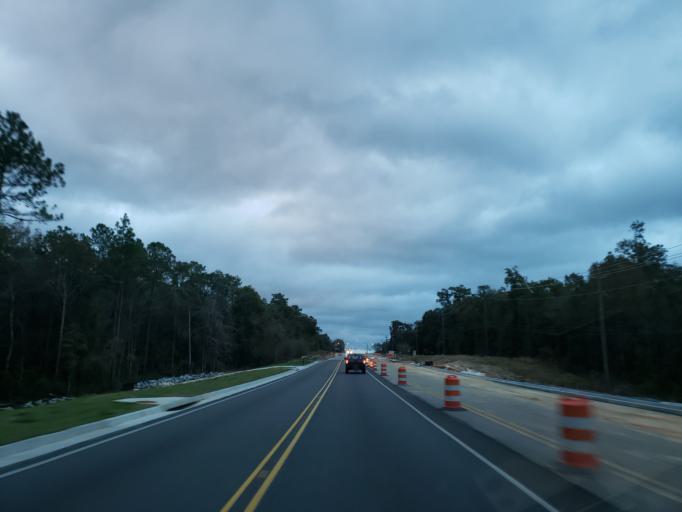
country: US
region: Alabama
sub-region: Mobile County
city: Chickasaw
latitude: 30.7879
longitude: -88.2258
